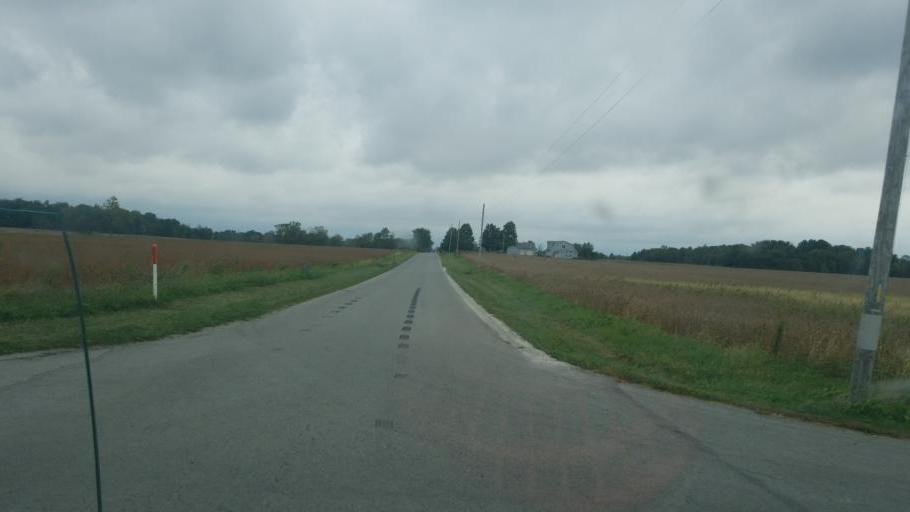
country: US
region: Ohio
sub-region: Seneca County
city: Fostoria
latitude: 41.0939
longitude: -83.5165
